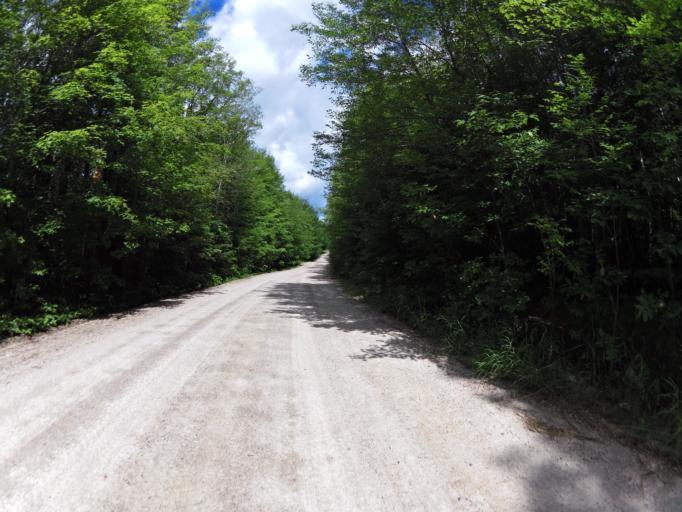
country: CA
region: Ontario
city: Perth
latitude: 45.0264
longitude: -76.5165
